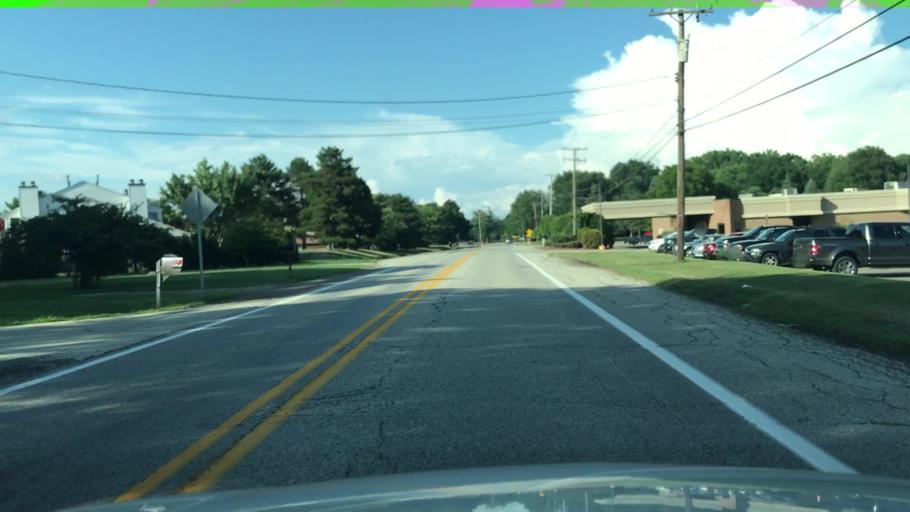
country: US
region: Michigan
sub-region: Macomb County
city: Clinton
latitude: 42.5818
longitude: -82.9434
